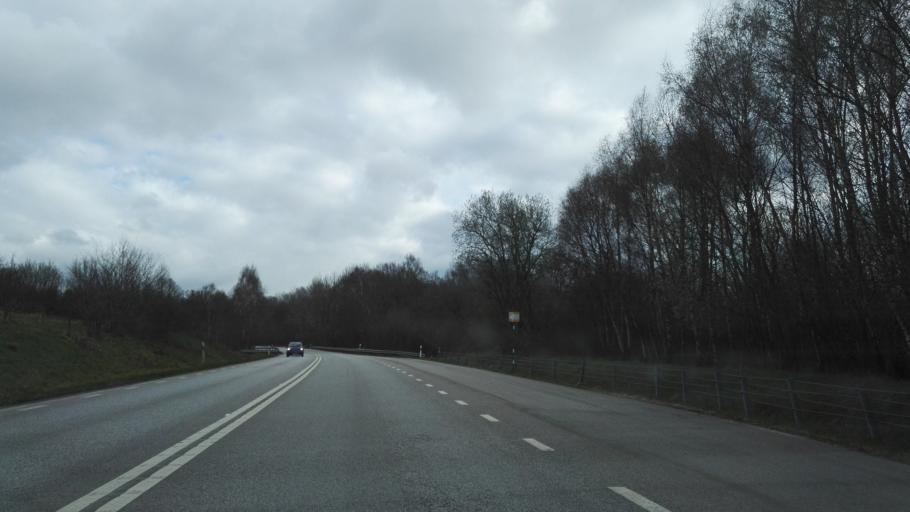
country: SE
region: Skane
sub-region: Horby Kommun
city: Hoerby
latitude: 55.8747
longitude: 13.6323
